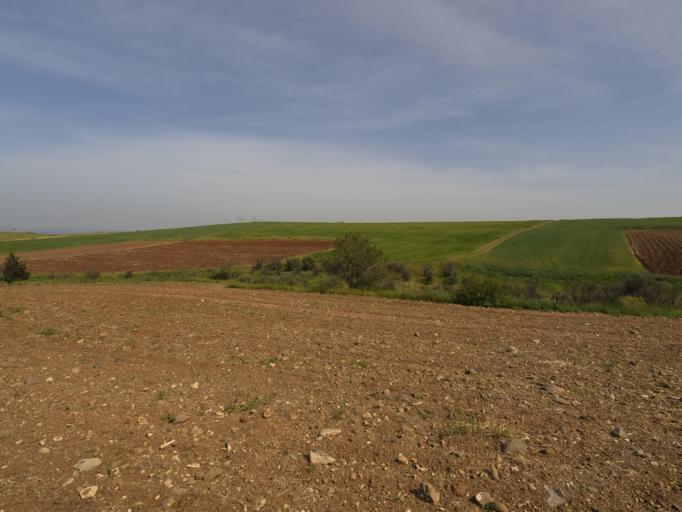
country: CY
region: Lefkosia
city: Astromeritis
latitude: 35.1036
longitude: 32.9627
